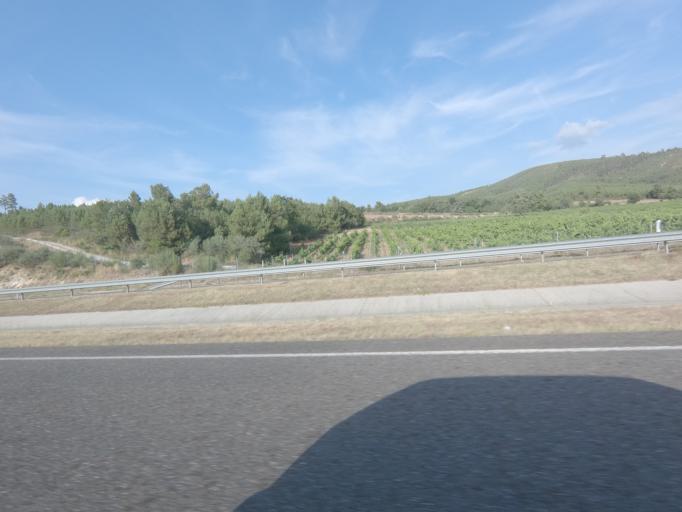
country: ES
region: Galicia
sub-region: Provincia de Ourense
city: Oimbra
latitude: 41.8708
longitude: -7.4333
